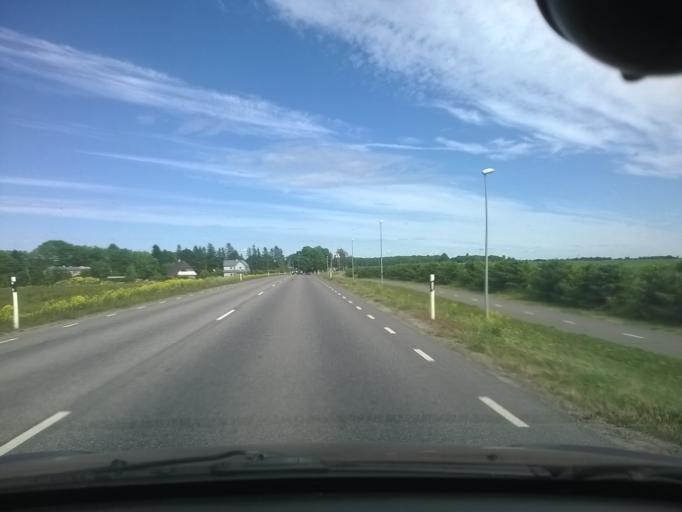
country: EE
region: Harju
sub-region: Rae vald
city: Jueri
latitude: 59.3609
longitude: 24.9596
